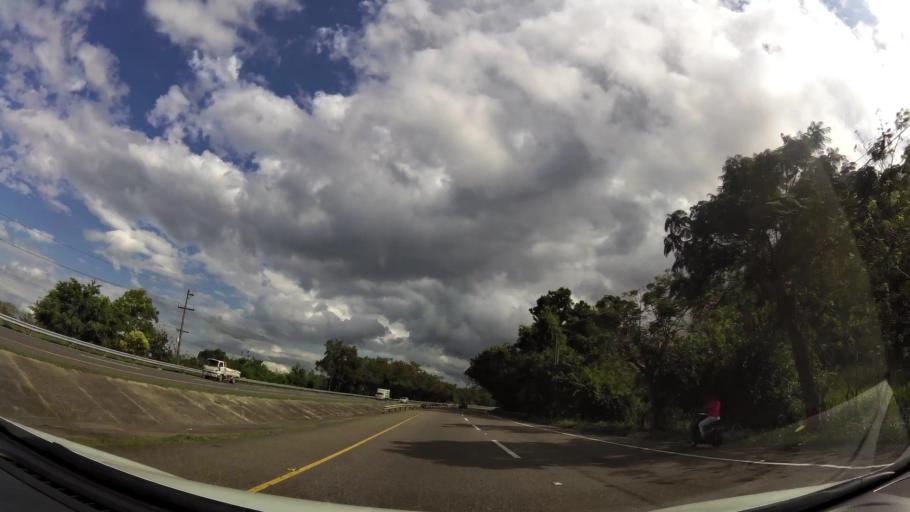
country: DO
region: La Vega
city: Concepcion de La Vega
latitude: 19.1652
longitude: -70.4865
